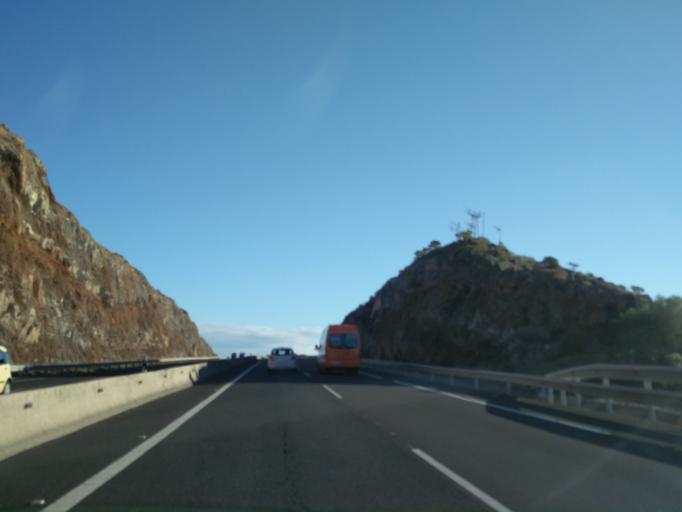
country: ES
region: Canary Islands
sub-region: Provincia de Santa Cruz de Tenerife
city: Fasnia
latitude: 28.2607
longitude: -16.3933
